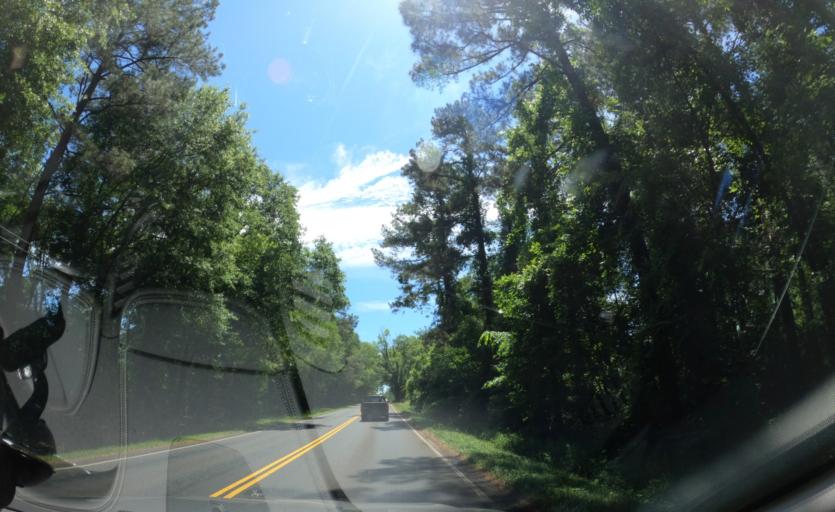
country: US
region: South Carolina
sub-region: McCormick County
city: McCormick
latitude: 33.9158
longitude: -82.3046
